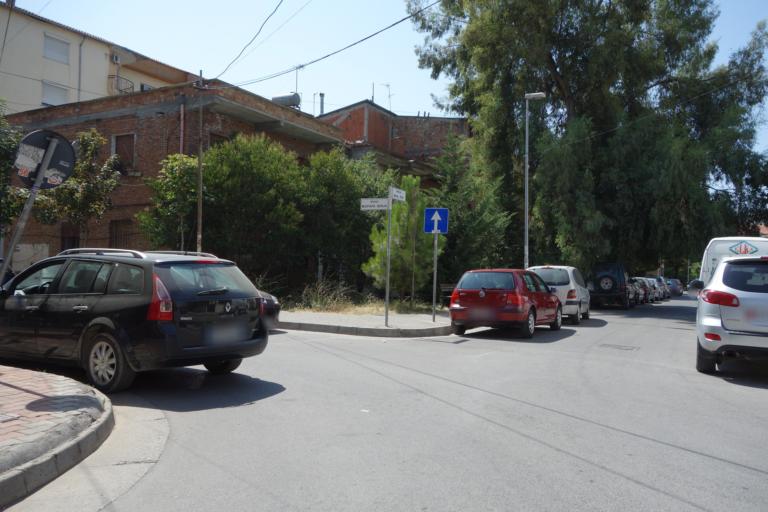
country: AL
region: Tirane
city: Tirana
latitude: 41.3203
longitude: 19.8088
